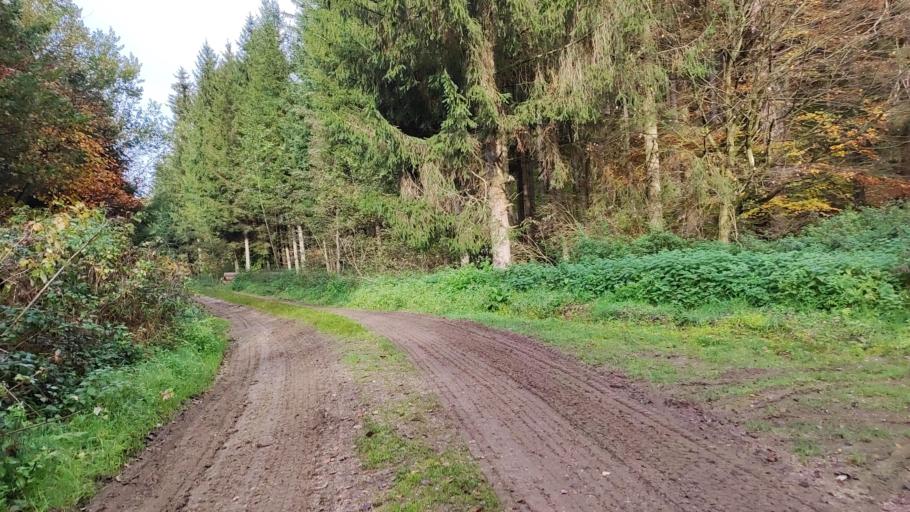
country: DE
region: Bavaria
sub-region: Swabia
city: Ziemetshausen
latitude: 48.2752
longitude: 10.5639
